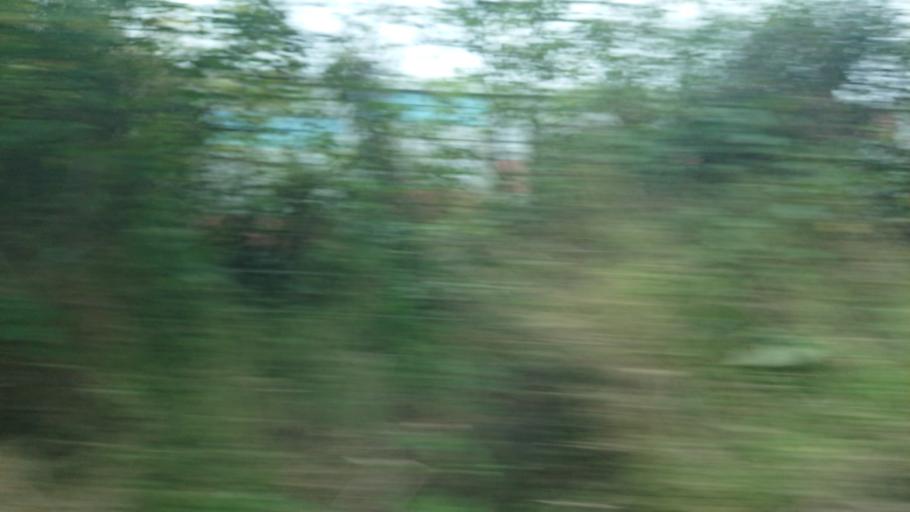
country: TW
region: Taiwan
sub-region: Hsinchu
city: Hsinchu
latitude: 24.8333
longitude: 120.9521
